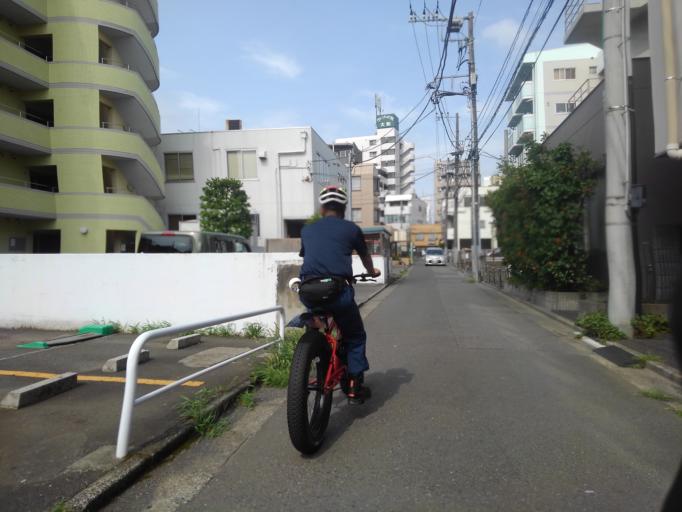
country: JP
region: Kanagawa
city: Minami-rinkan
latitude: 35.4717
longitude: 139.4641
